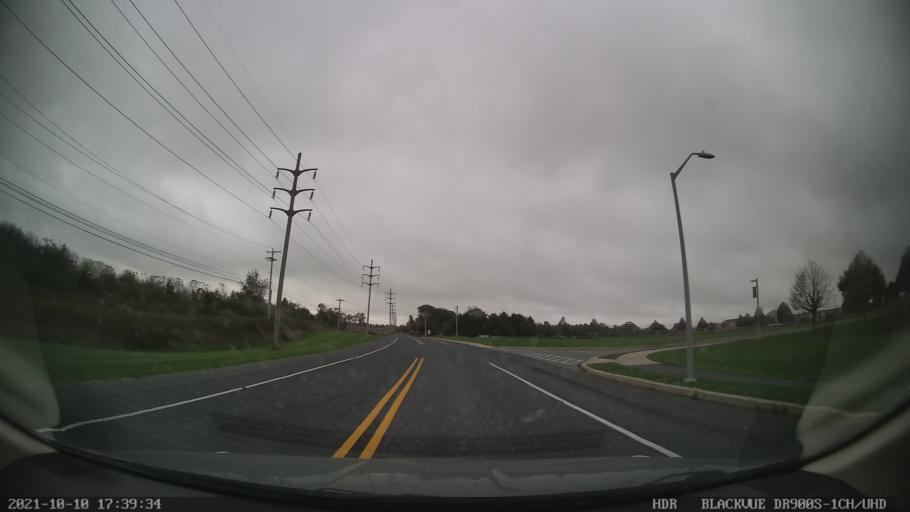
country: US
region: Pennsylvania
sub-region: Berks County
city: Topton
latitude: 40.5087
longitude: -75.6966
